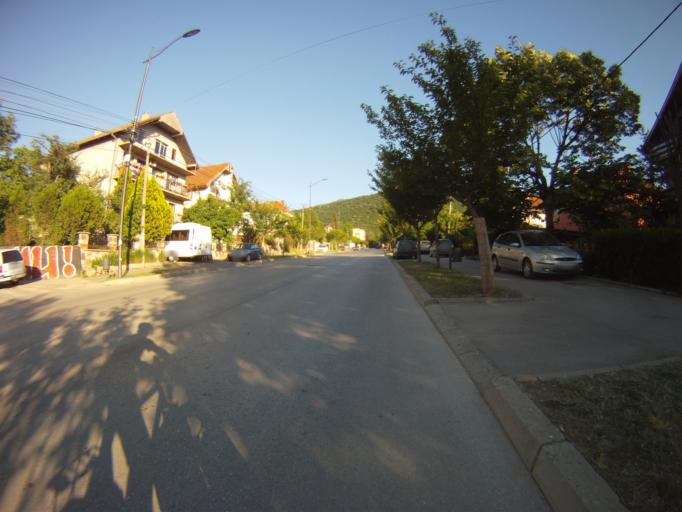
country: RS
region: Central Serbia
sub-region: Nisavski Okrug
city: Niska Banja
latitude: 43.2961
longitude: 22.0025
